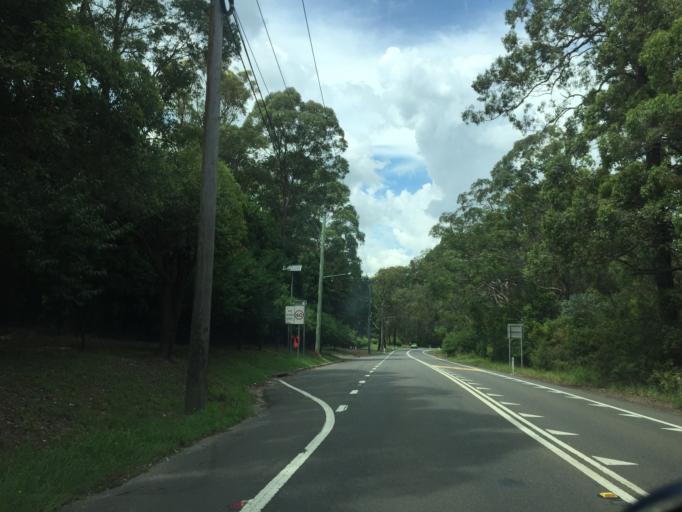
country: AU
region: New South Wales
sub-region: Hornsby Shire
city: Galston
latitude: -33.6610
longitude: 151.0394
